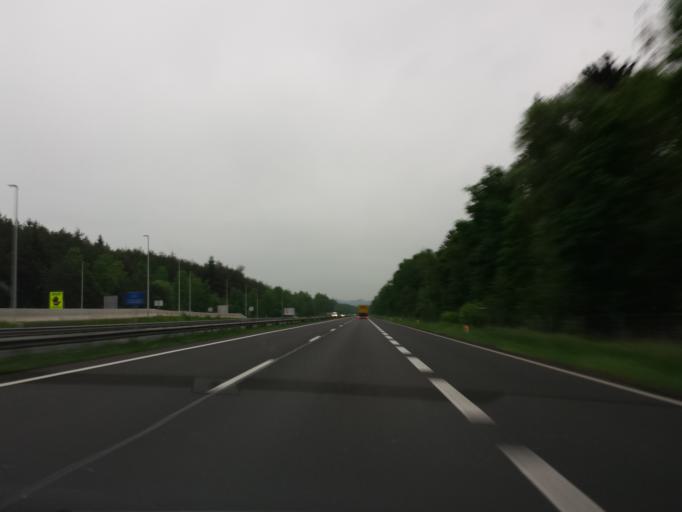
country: AT
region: Styria
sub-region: Politischer Bezirk Hartberg-Fuerstenfeld
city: Hainersdorf
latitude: 47.1164
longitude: 15.9842
